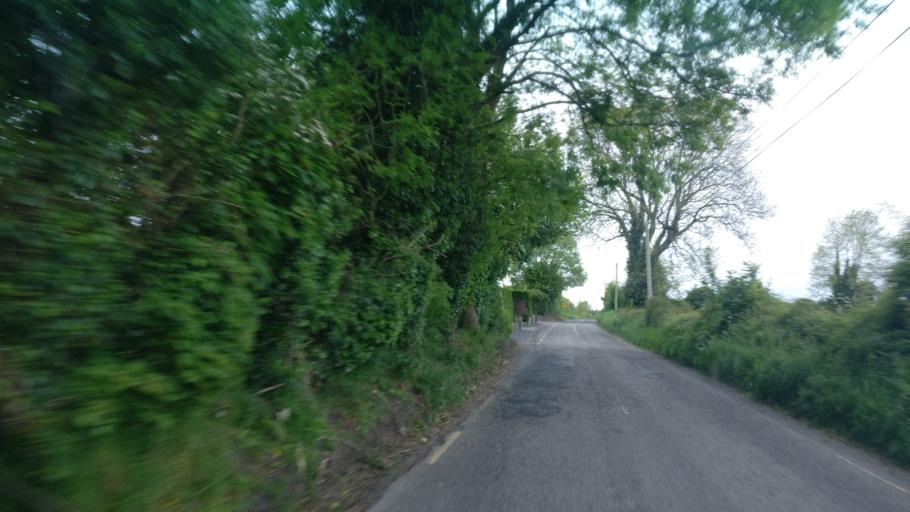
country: IE
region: Connaught
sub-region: County Galway
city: Portumna
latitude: 53.1029
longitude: -8.2549
